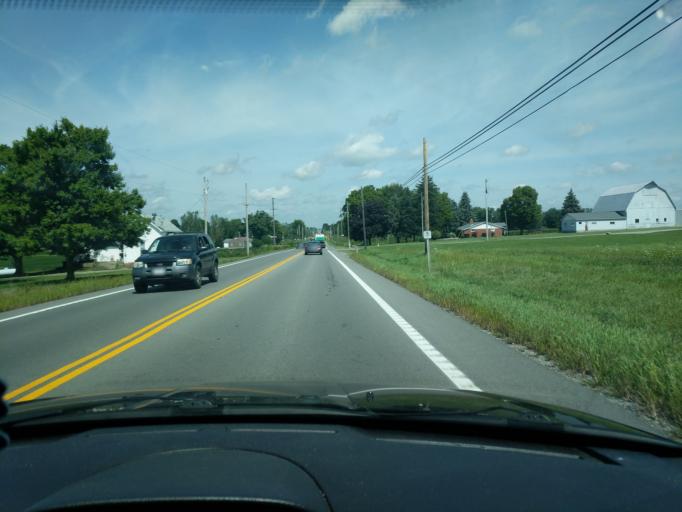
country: US
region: Ohio
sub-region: Logan County
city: Bellefontaine
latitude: 40.3130
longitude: -83.7601
